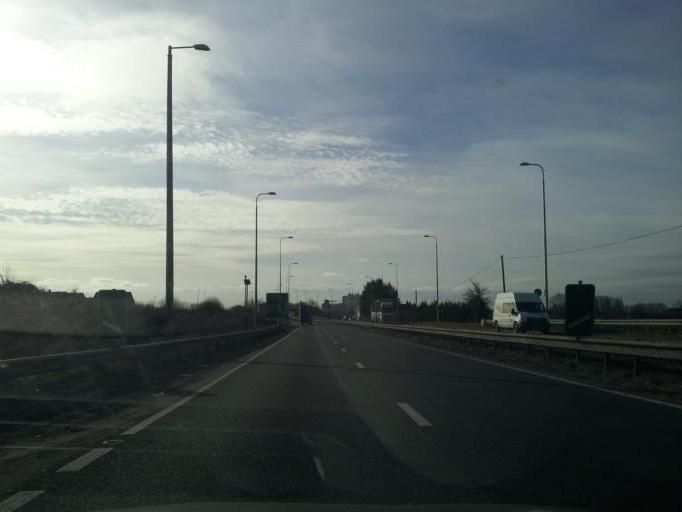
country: GB
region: England
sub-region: Central Bedfordshire
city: Sandy
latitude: 52.1426
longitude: -0.3006
